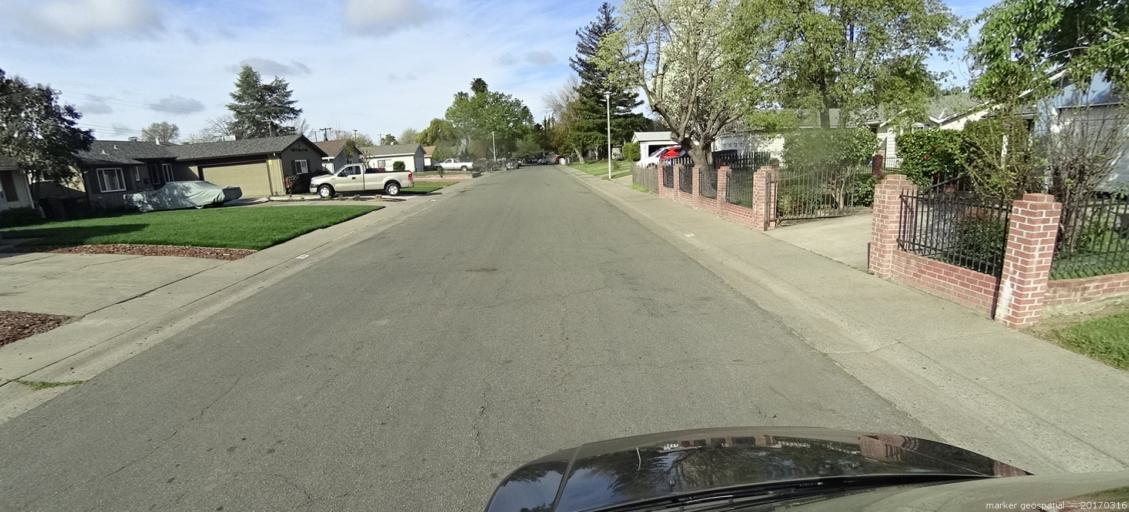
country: US
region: California
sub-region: Sacramento County
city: Parkway
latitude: 38.5059
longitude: -121.4863
